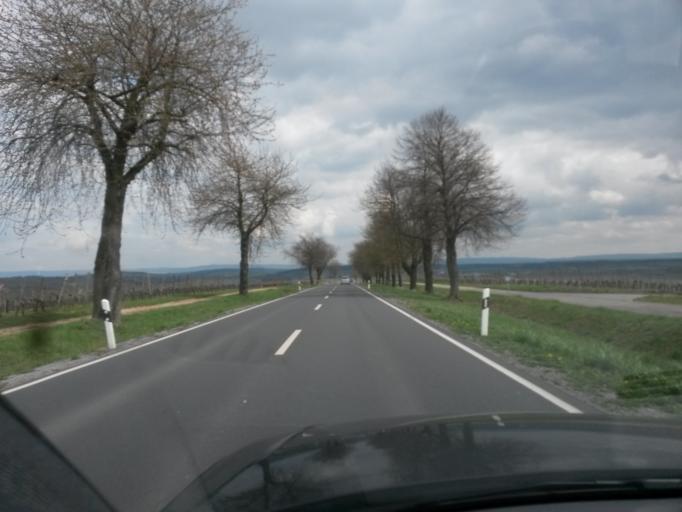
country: DE
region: Bavaria
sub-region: Regierungsbezirk Unterfranken
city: Nordheim
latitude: 49.8674
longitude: 10.1911
